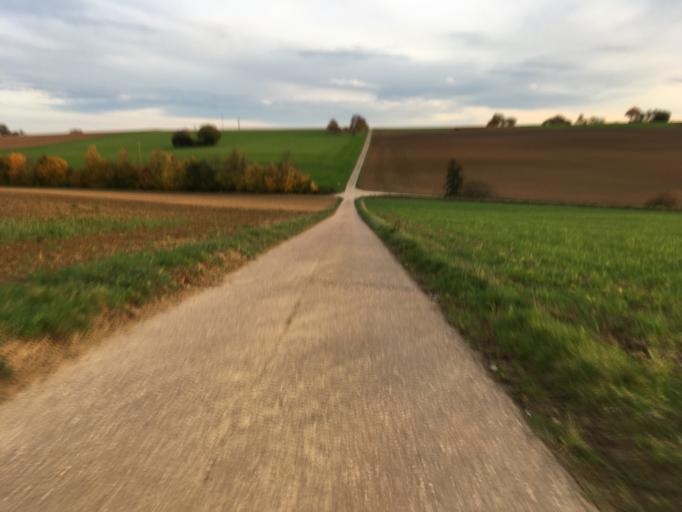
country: DE
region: Baden-Wuerttemberg
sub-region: Regierungsbezirk Stuttgart
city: Kirchardt
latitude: 49.2360
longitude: 8.9889
